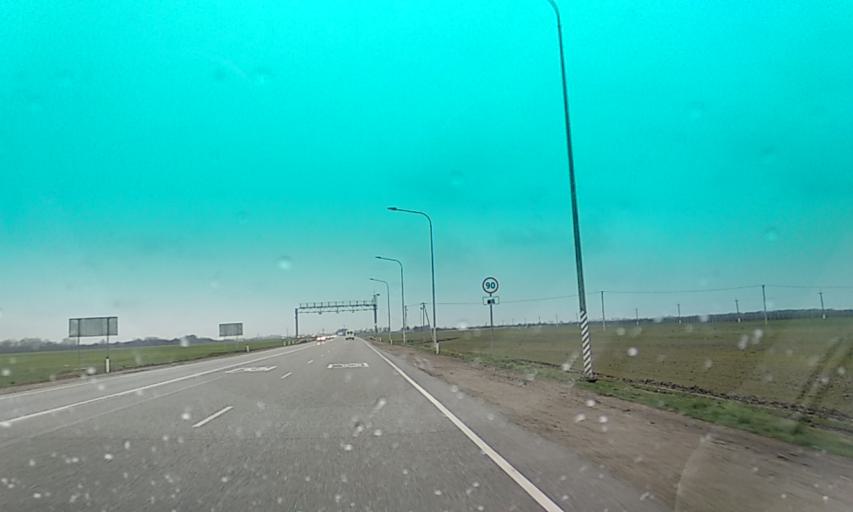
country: RU
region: Krasnodarskiy
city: Belorechensk
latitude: 44.8270
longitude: 39.8450
